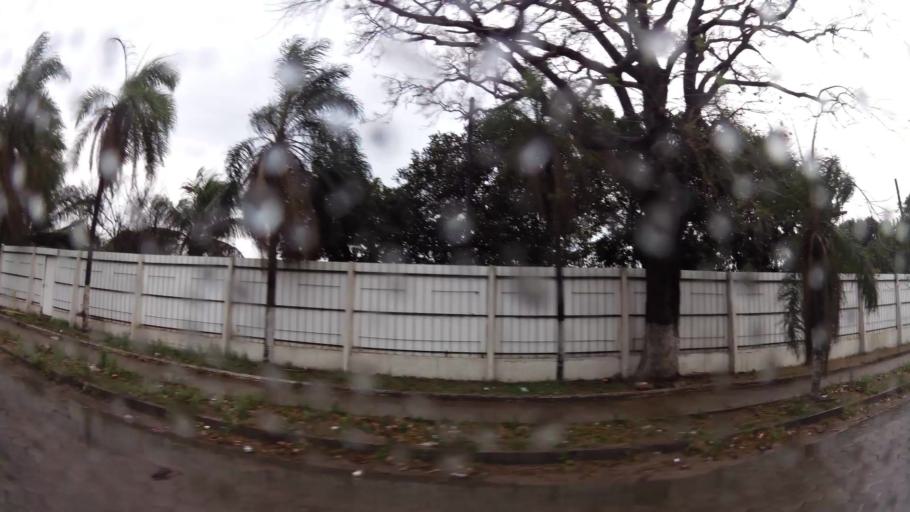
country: BO
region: Santa Cruz
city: Santa Cruz de la Sierra
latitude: -17.7638
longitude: -63.1418
